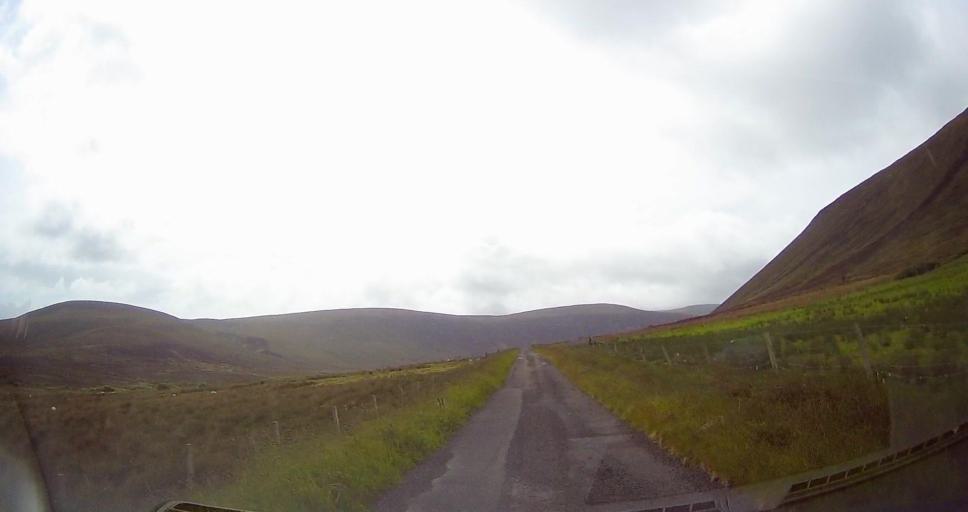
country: GB
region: Scotland
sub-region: Orkney Islands
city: Stromness
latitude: 58.9021
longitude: -3.3163
